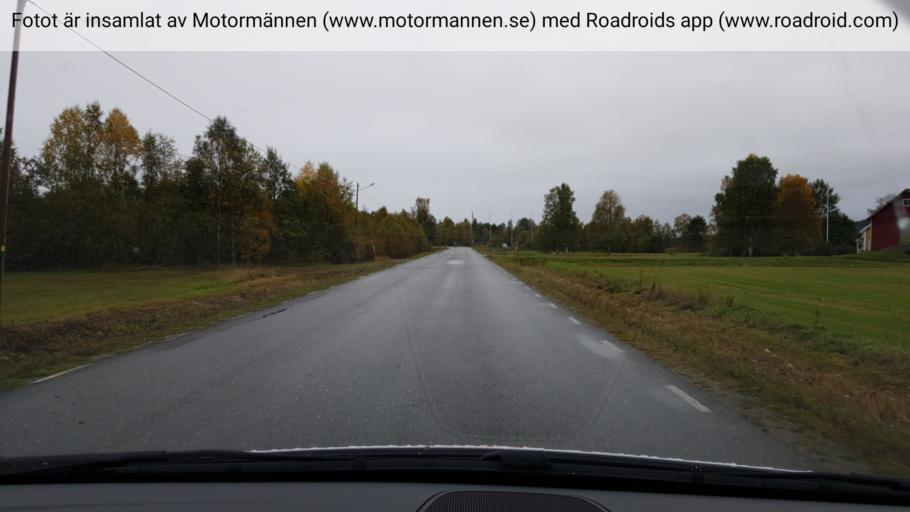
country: SE
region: Vaesterbotten
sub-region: Vannas Kommun
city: Vannasby
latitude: 63.9257
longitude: 19.8558
